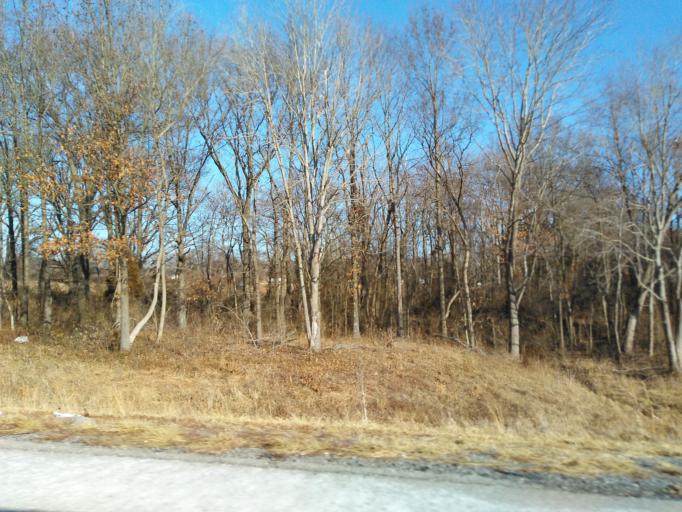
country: US
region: Illinois
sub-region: Franklin County
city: Benton
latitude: 38.0549
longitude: -88.9243
